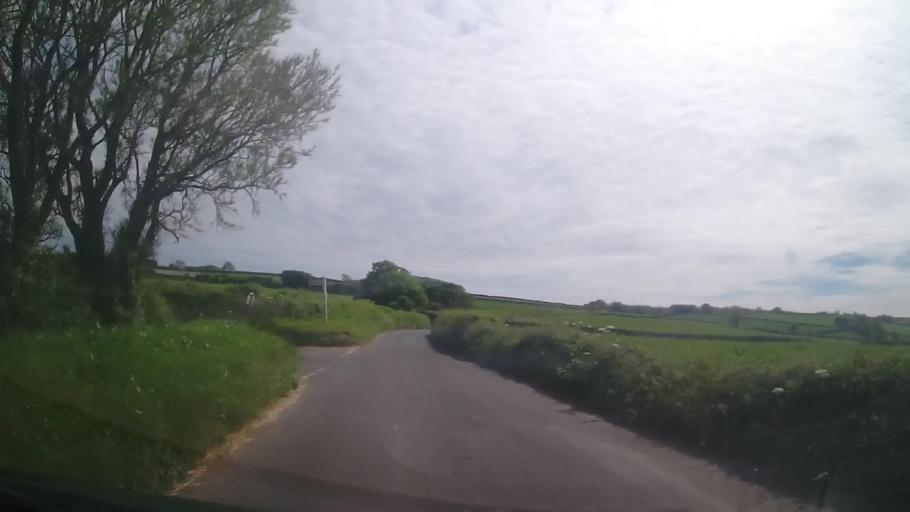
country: GB
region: England
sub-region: Devon
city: Salcombe
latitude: 50.2588
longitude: -3.6772
